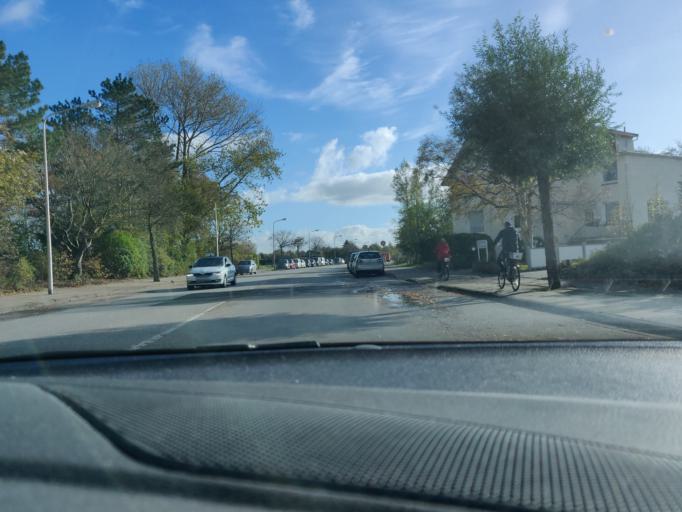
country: DE
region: Lower Saxony
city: Cuxhaven
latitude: 53.8810
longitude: 8.6724
